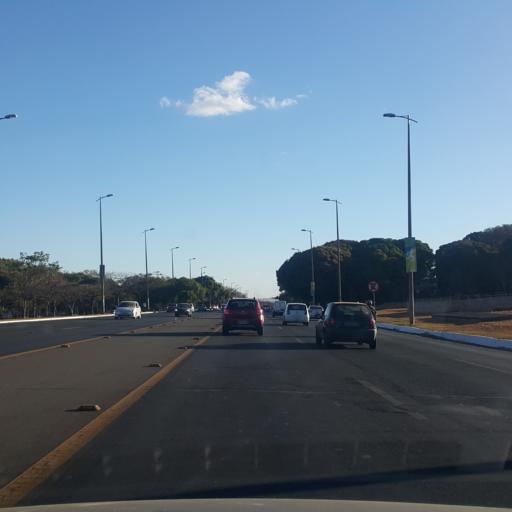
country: BR
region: Federal District
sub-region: Brasilia
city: Brasilia
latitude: -15.8147
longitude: -47.8978
